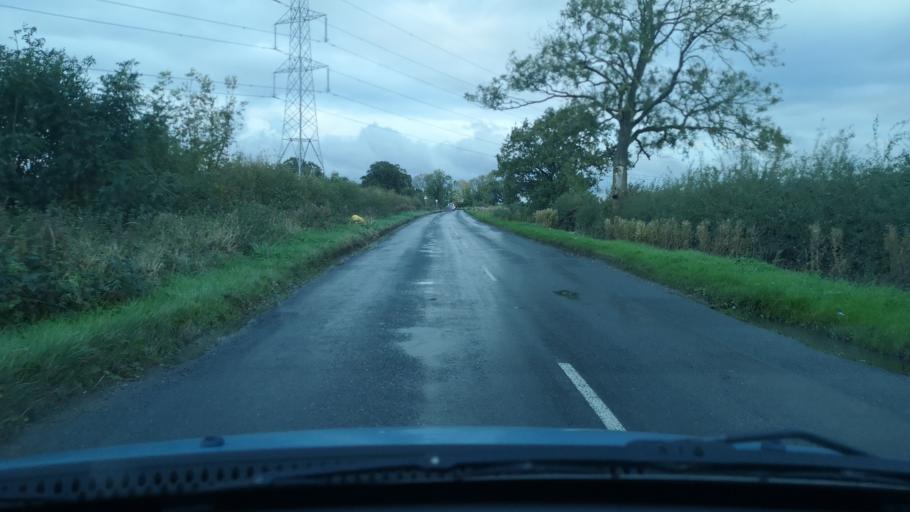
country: GB
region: England
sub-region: Doncaster
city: Moss
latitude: 53.6210
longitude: -1.0800
